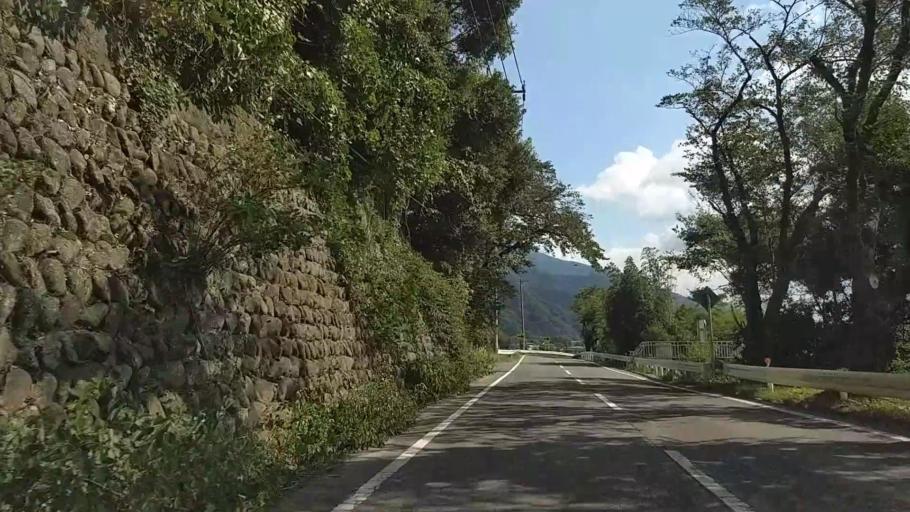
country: JP
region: Shizuoka
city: Fujinomiya
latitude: 35.3955
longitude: 138.4495
